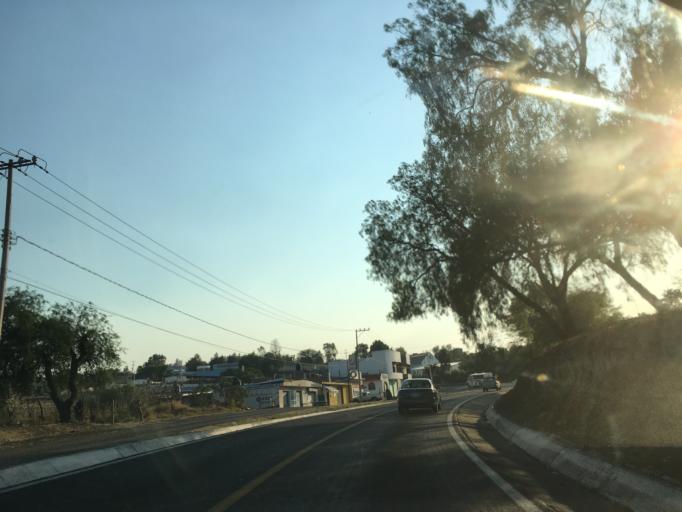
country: MX
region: Michoacan
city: Charo
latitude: 19.7513
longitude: -101.0481
